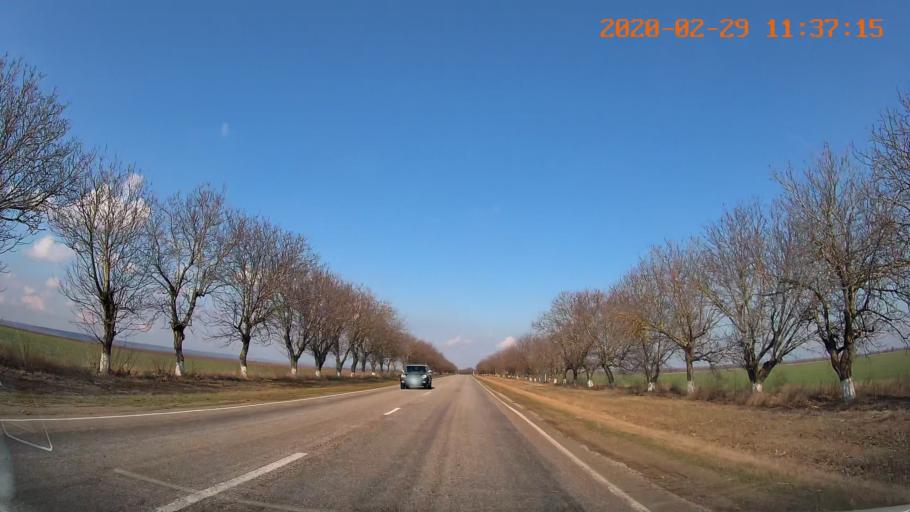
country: MD
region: Rezina
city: Saharna
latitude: 47.6088
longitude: 29.0477
